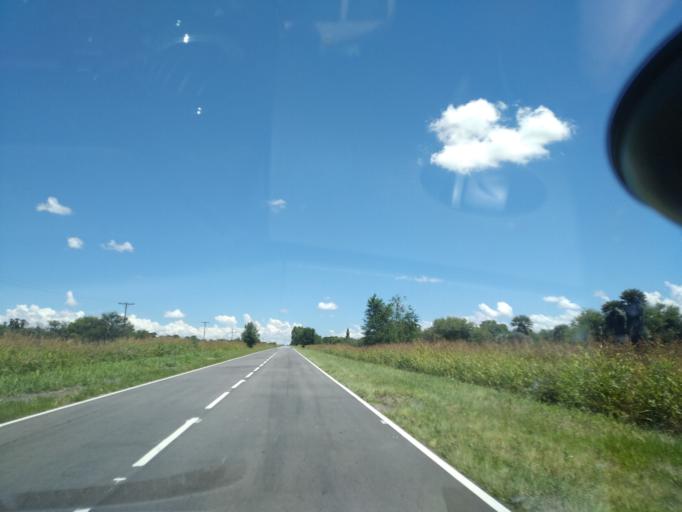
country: AR
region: Cordoba
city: Salsacate
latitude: -31.3842
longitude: -65.0997
